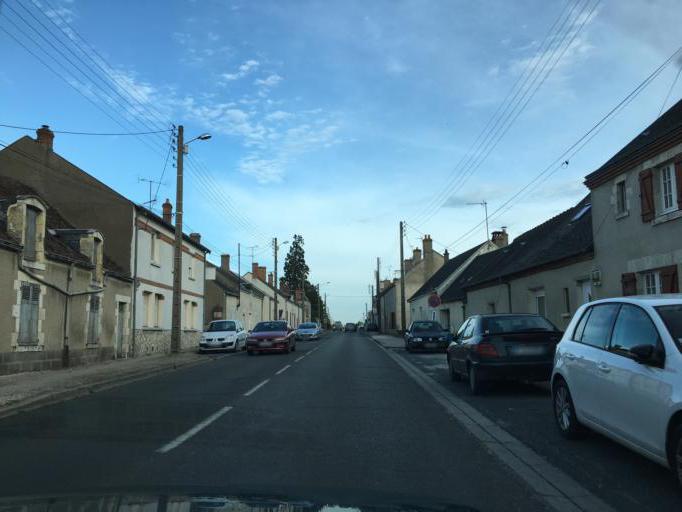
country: FR
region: Centre
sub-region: Departement du Loiret
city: Saint-Jean-de-la-Ruelle
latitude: 47.9223
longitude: 1.8518
